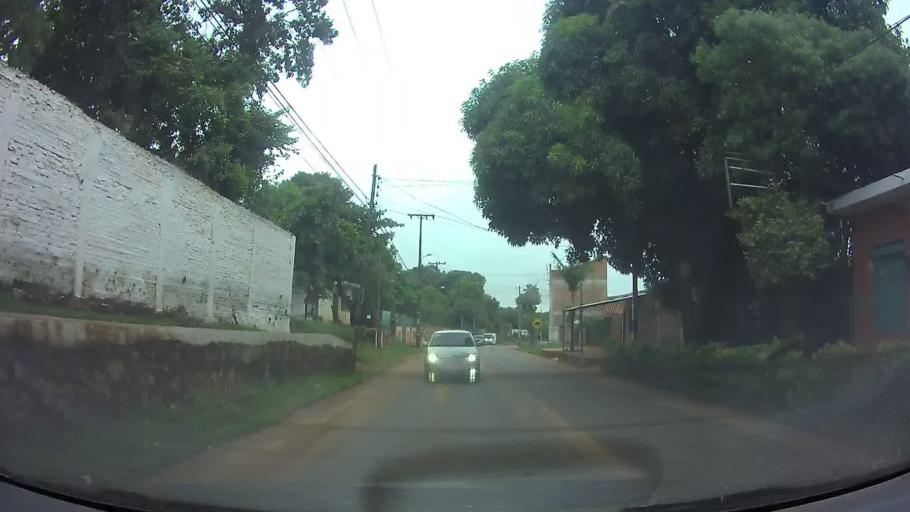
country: PY
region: Central
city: San Lorenzo
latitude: -25.3061
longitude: -57.4908
